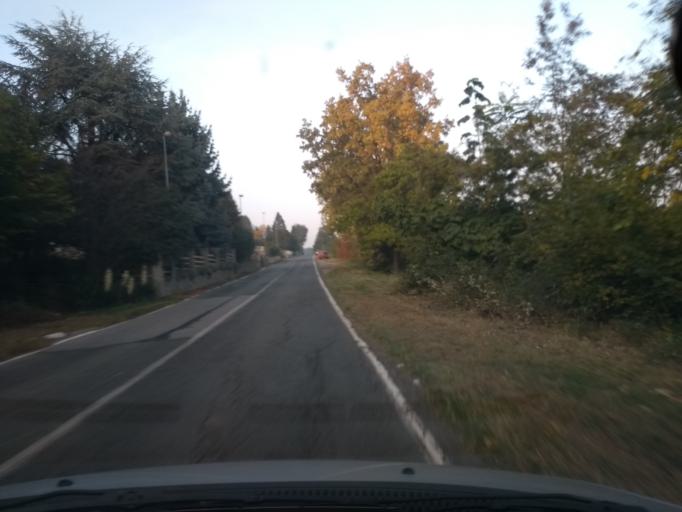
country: IT
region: Piedmont
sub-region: Provincia di Torino
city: Givoletto
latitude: 45.1629
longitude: 7.5012
